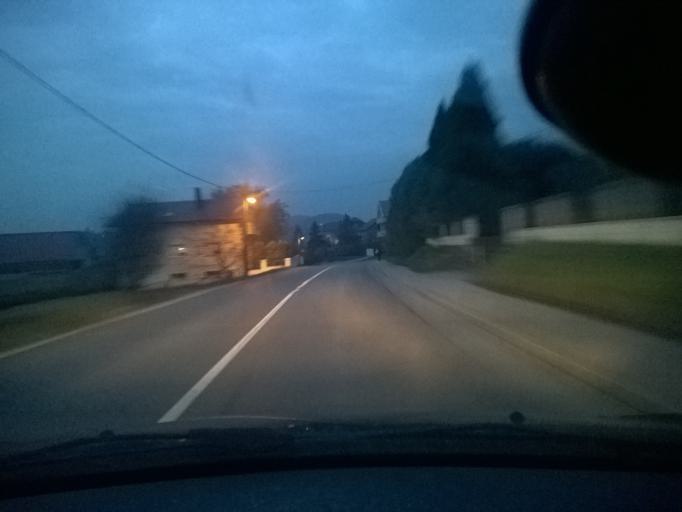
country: HR
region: Krapinsko-Zagorska
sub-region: Grad Krapina
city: Krapina
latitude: 46.1361
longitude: 15.8835
